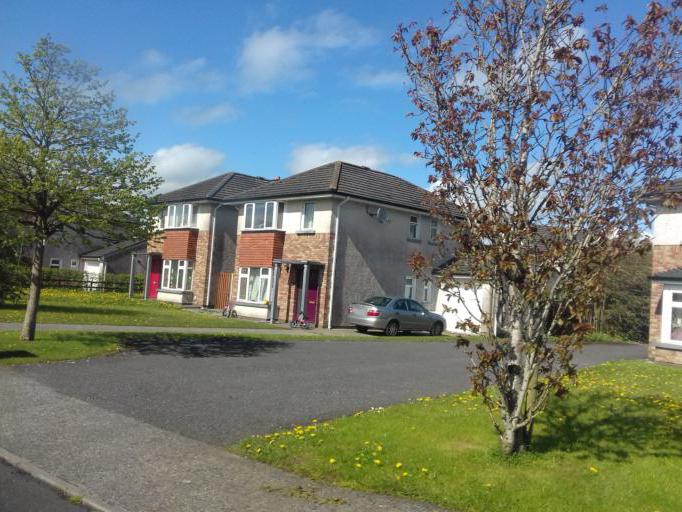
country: IE
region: Leinster
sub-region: Laois
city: Portlaoise
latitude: 53.0440
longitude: -7.2708
